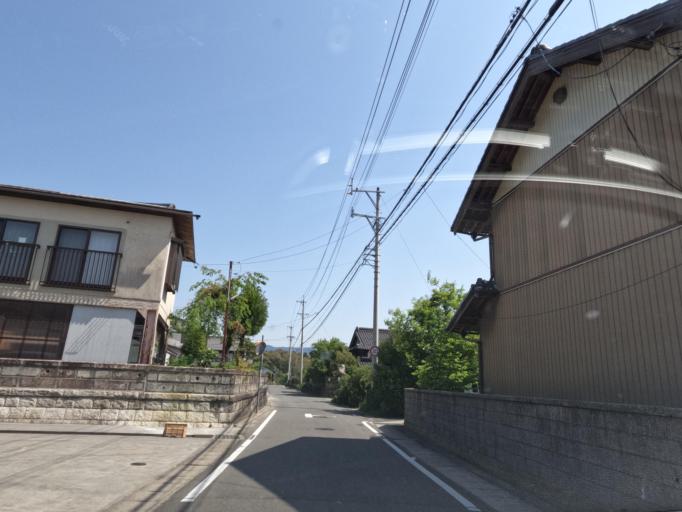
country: JP
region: Mie
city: Komono
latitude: 35.1598
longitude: 136.5002
